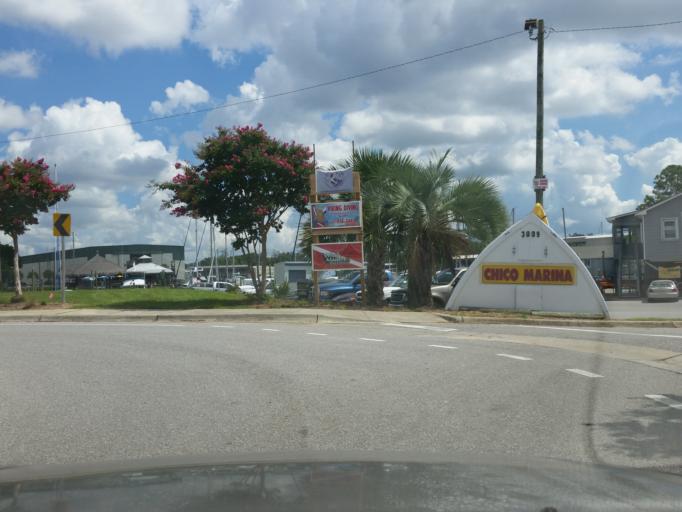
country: US
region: Florida
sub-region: Escambia County
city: Warrington
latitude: 30.3985
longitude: -87.2433
